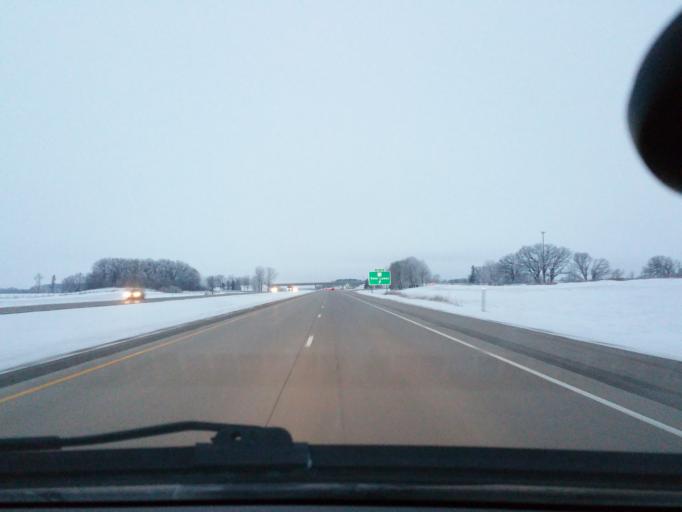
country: US
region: Minnesota
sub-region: Freeborn County
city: Albert Lea
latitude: 43.5817
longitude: -93.3583
